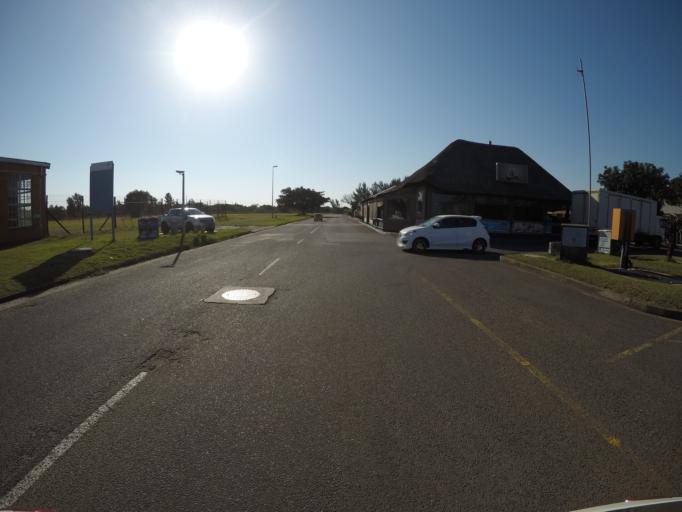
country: ZA
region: KwaZulu-Natal
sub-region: uThungulu District Municipality
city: Richards Bay
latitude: -28.7934
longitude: 32.0778
